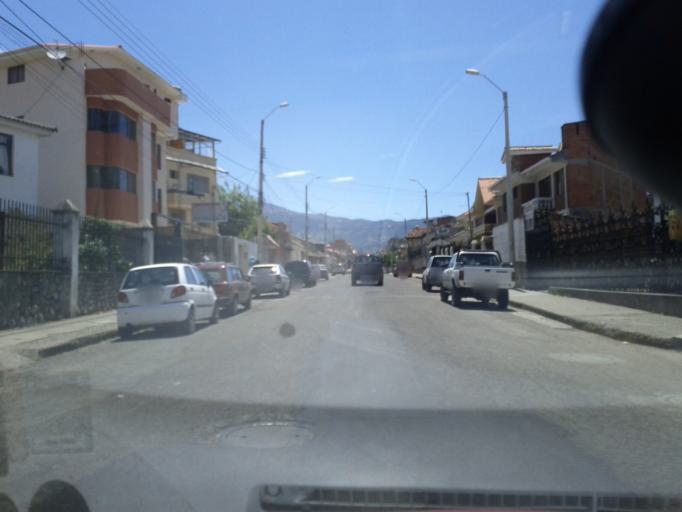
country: EC
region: Azuay
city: Cuenca
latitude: -2.9080
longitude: -79.0137
